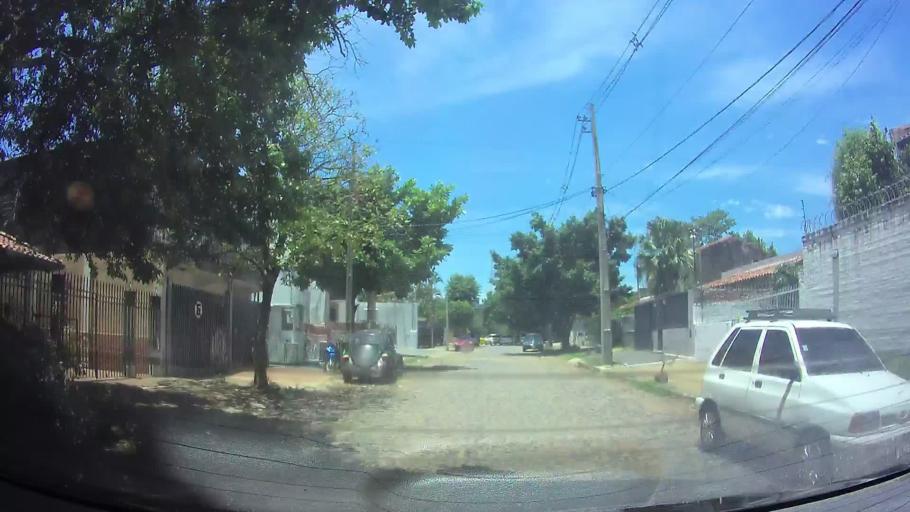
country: PY
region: Asuncion
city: Asuncion
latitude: -25.2710
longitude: -57.6006
